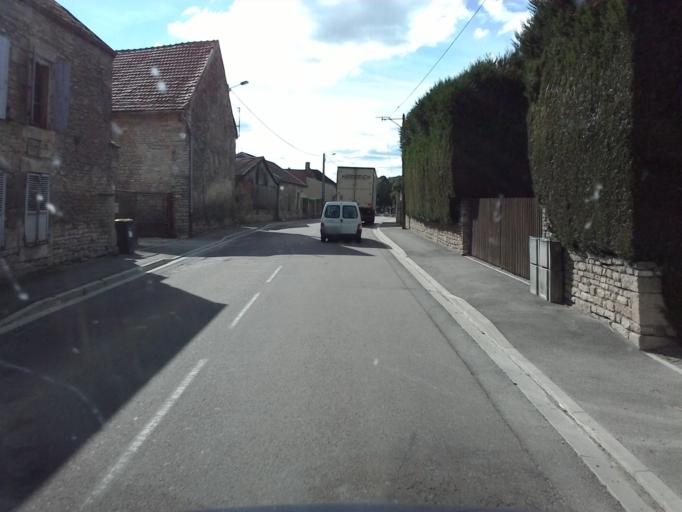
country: FR
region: Bourgogne
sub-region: Departement de la Cote-d'Or
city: Chatillon-sur-Seine
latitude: 47.7505
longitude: 4.4953
